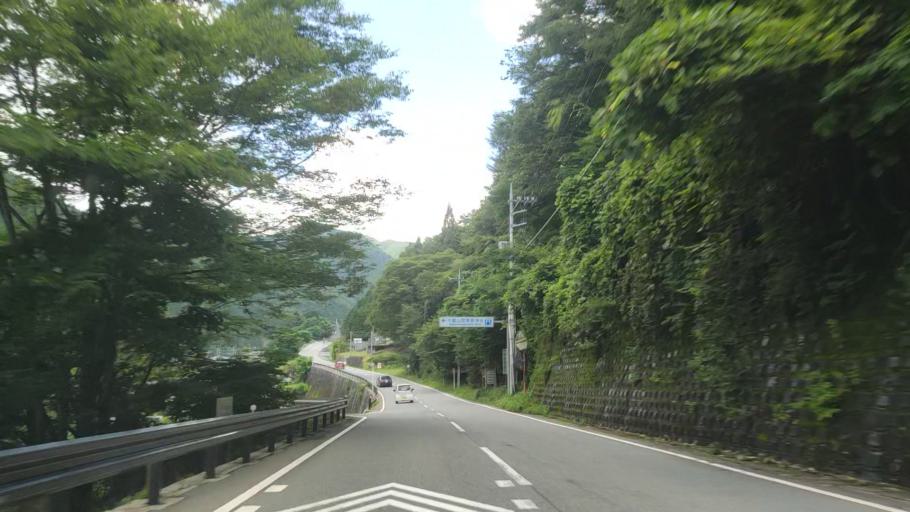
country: JP
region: Yamanashi
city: Enzan
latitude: 35.8070
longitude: 138.7512
